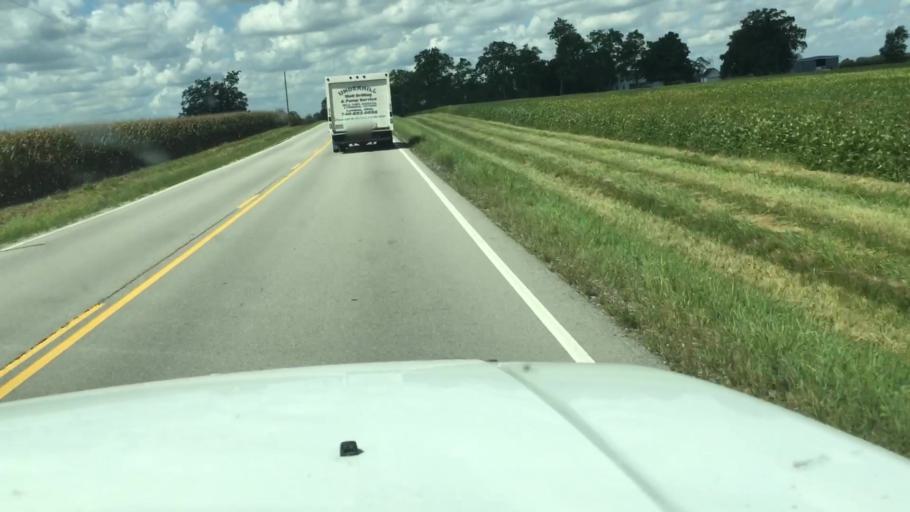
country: US
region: Ohio
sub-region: Madison County
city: Bethel
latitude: 39.8044
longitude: -83.3319
